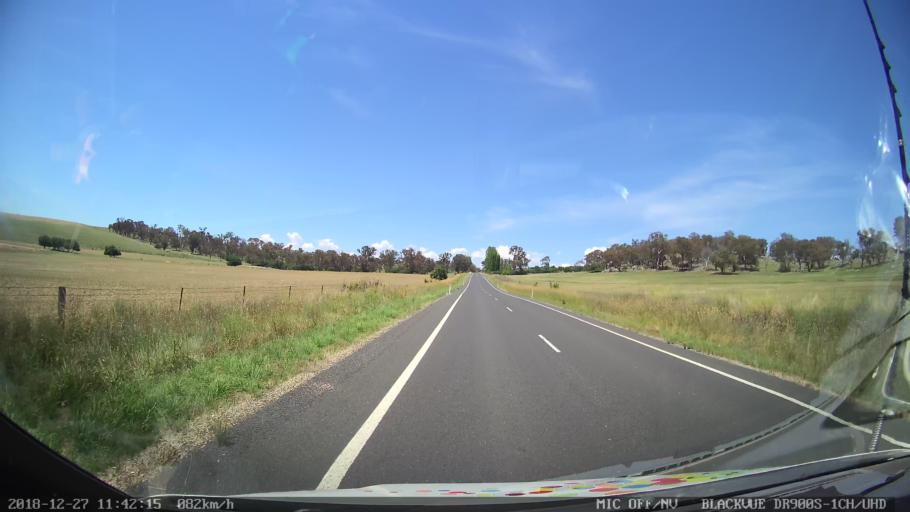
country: AU
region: New South Wales
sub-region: Bathurst Regional
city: Perthville
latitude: -33.5464
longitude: 149.4790
